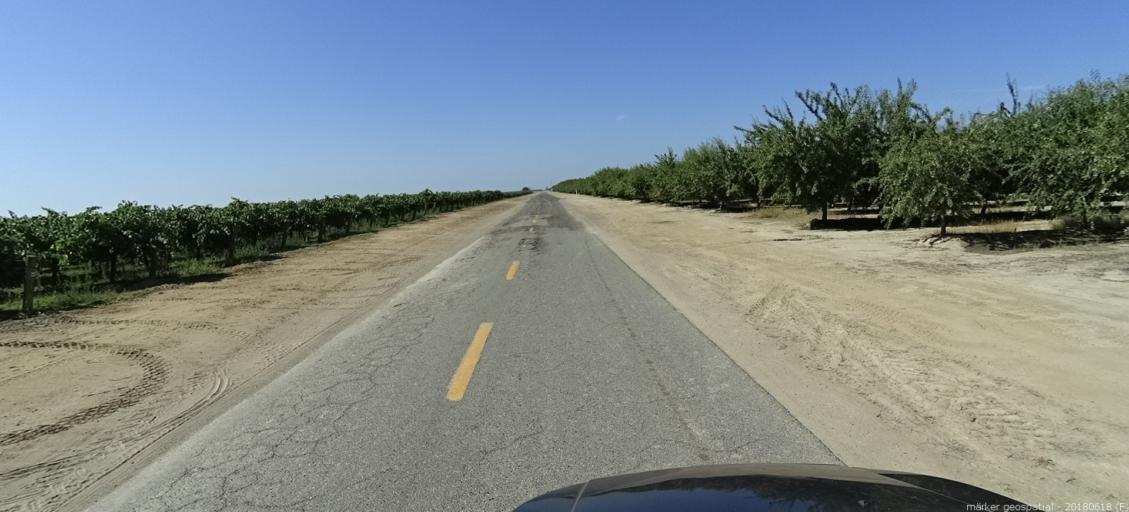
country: US
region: California
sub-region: Madera County
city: Parkwood
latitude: 36.8635
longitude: -120.1465
